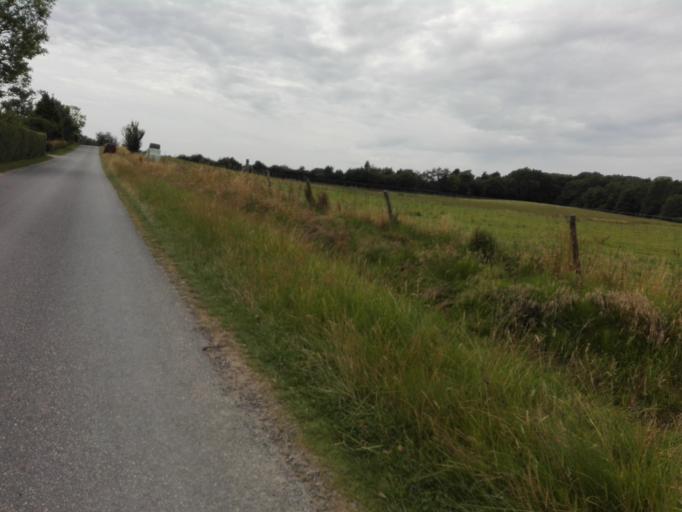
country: DK
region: Central Jutland
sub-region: Arhus Kommune
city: Beder
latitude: 56.0475
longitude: 10.2633
